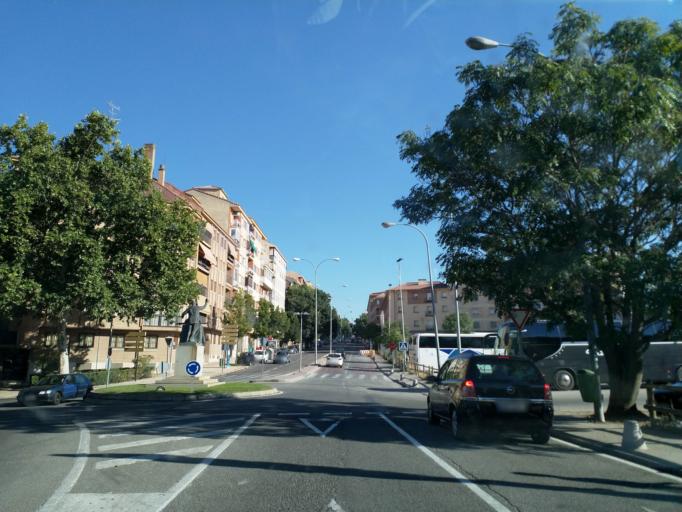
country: ES
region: Castille and Leon
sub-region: Provincia de Segovia
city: Segovia
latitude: 40.9472
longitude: -4.1243
